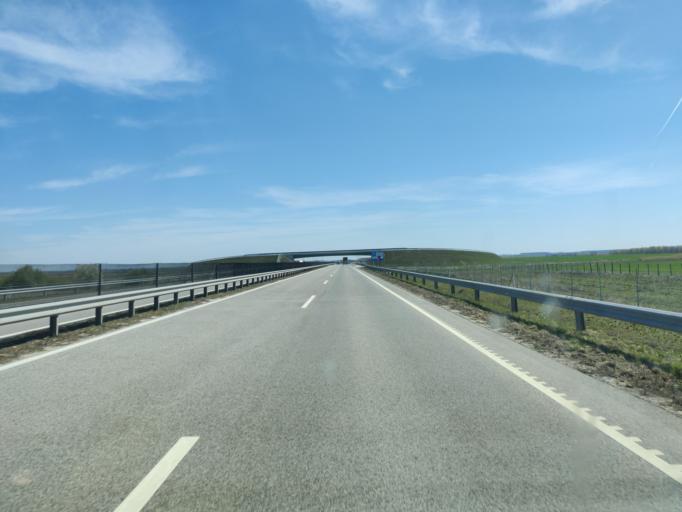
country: HU
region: Jasz-Nagykun-Szolnok
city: Cserkeszolo
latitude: 46.8845
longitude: 20.2081
